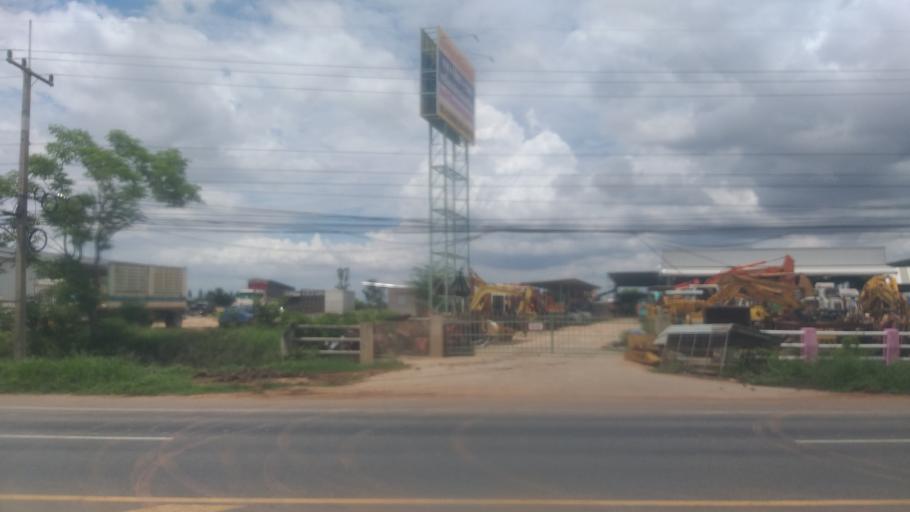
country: TH
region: Nakhon Ratchasima
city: Non Thai
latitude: 15.1004
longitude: 102.1051
